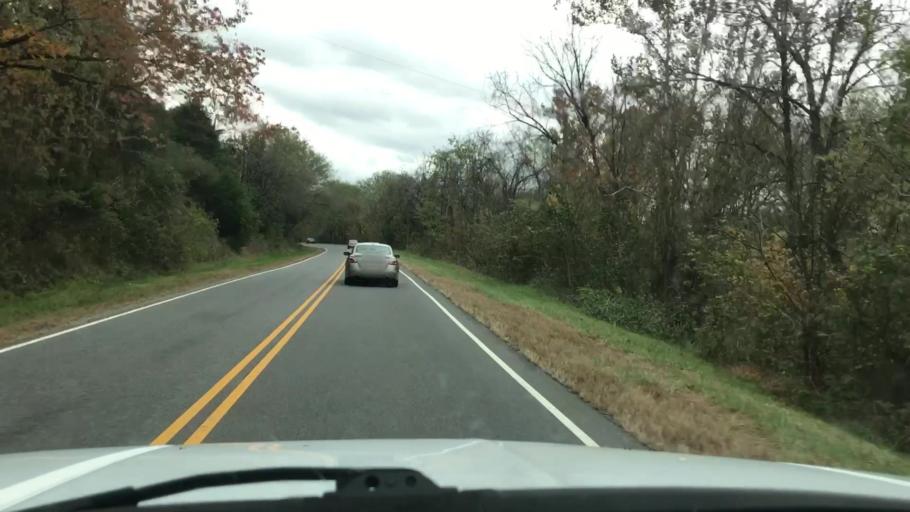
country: US
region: Virginia
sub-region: Goochland County
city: Goochland
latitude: 37.6200
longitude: -77.7664
